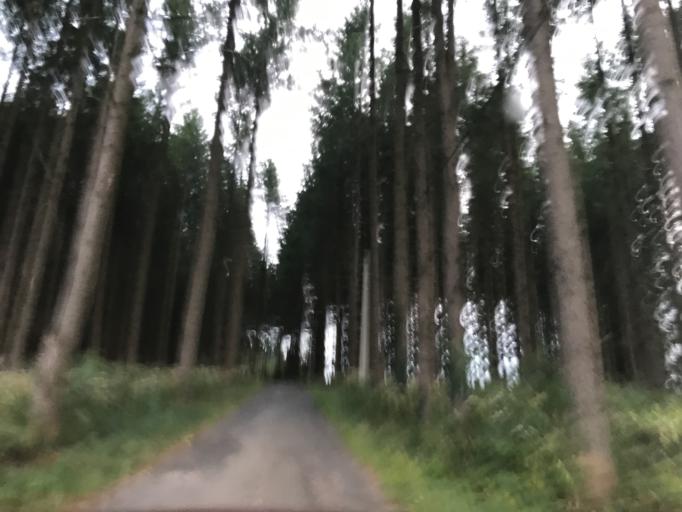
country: FR
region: Auvergne
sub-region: Departement du Puy-de-Dome
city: La Monnerie-le-Montel
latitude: 45.8494
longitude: 3.5983
